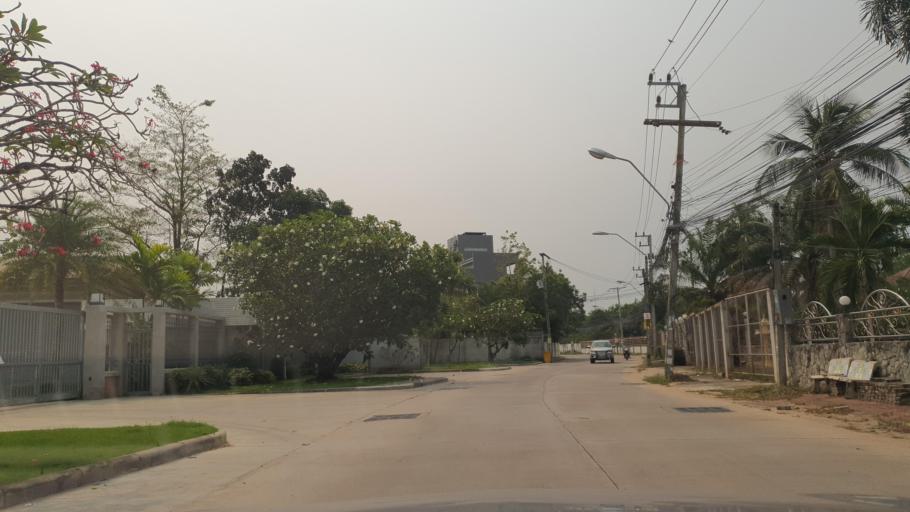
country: TH
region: Chon Buri
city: Phatthaya
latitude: 12.8928
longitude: 100.8911
